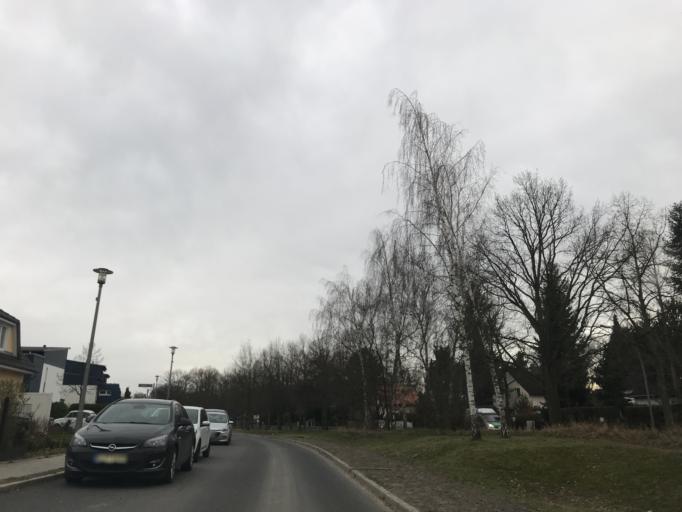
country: DE
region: Berlin
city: Kladow
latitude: 52.4698
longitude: 13.1247
